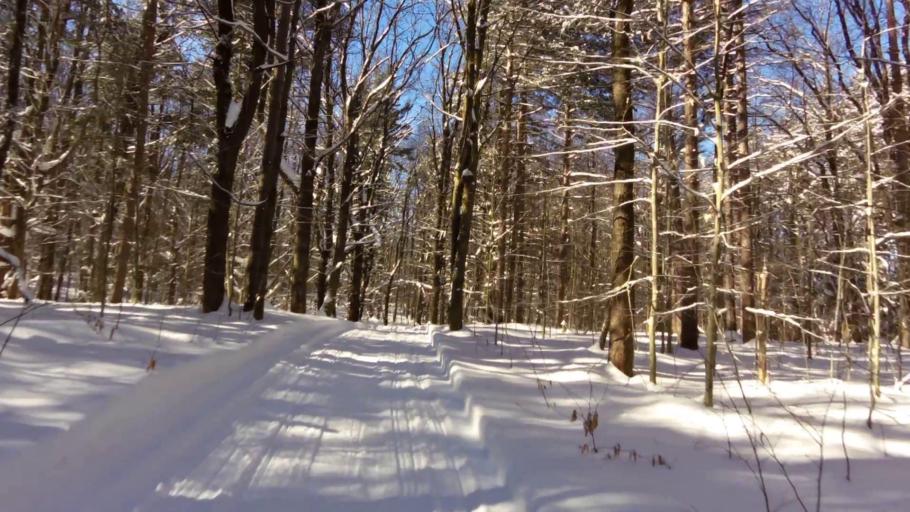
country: US
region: New York
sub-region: Chautauqua County
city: Fredonia
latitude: 42.3482
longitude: -79.1884
